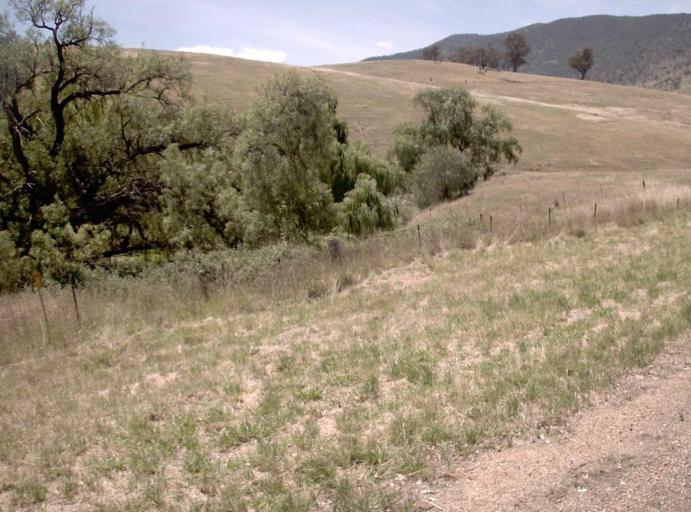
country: AU
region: Victoria
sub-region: East Gippsland
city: Bairnsdale
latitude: -37.1852
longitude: 147.7169
